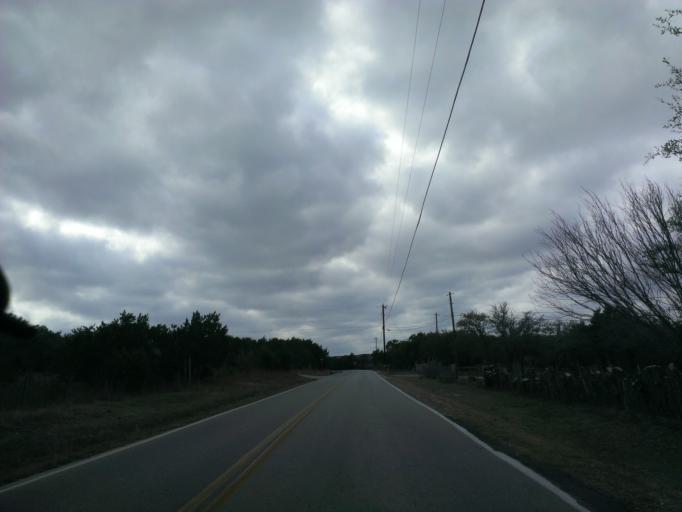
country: US
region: Texas
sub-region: Travis County
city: Briarcliff
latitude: 30.3768
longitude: -98.0860
